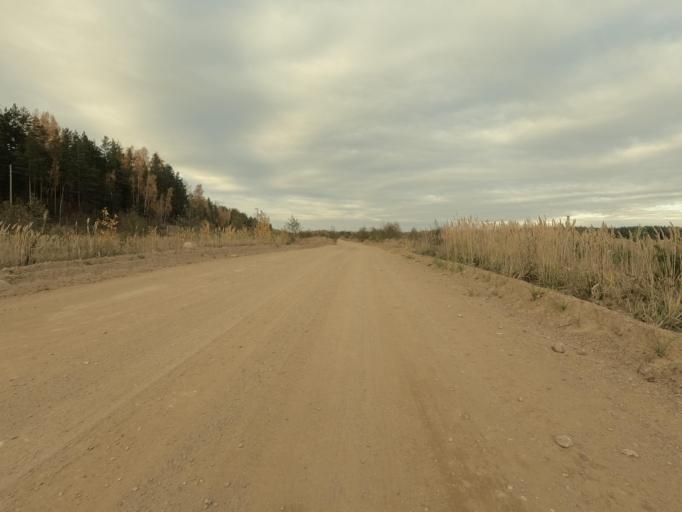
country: RU
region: Leningrad
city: Priladozhskiy
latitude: 59.7041
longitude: 31.3637
